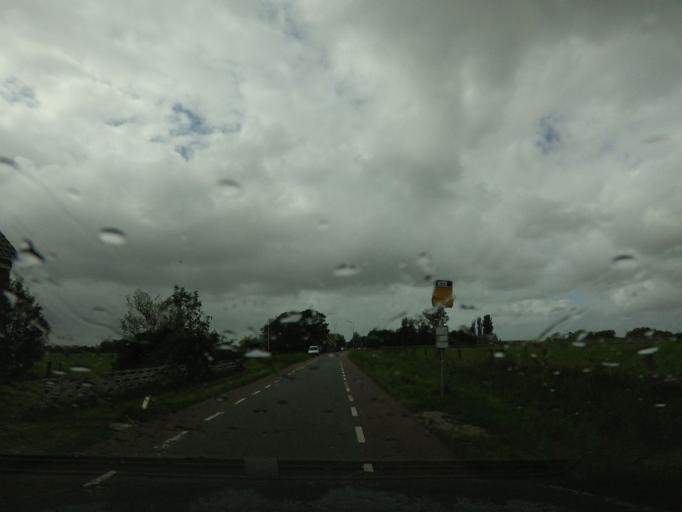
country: NL
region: North Holland
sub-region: Gemeente Schagen
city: Harenkarspel
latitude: 52.7399
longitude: 4.7246
